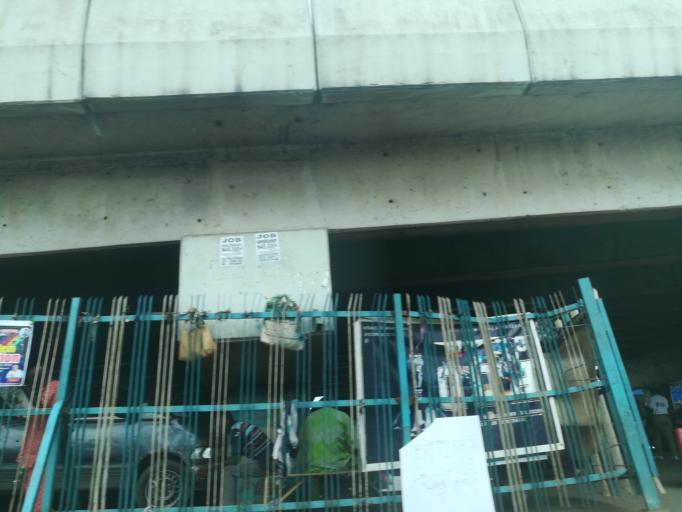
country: NG
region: Lagos
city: Ojota
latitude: 6.6061
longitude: 3.3996
